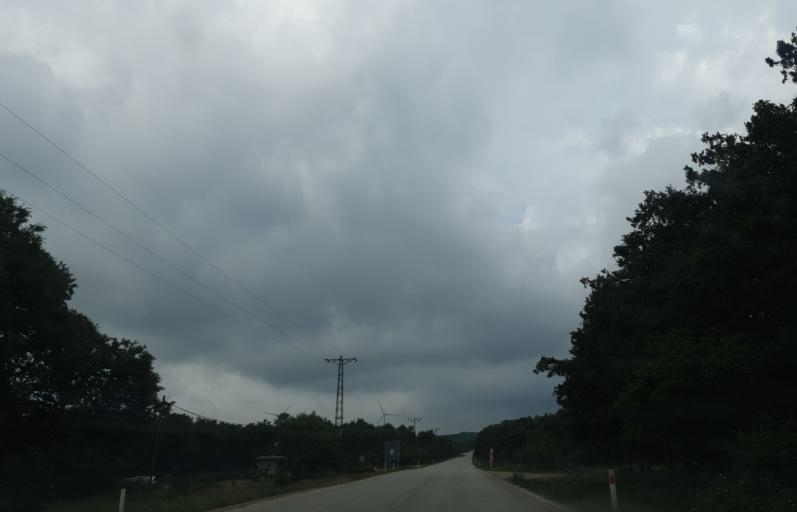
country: TR
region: Tekirdag
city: Saray
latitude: 41.4983
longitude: 27.9909
